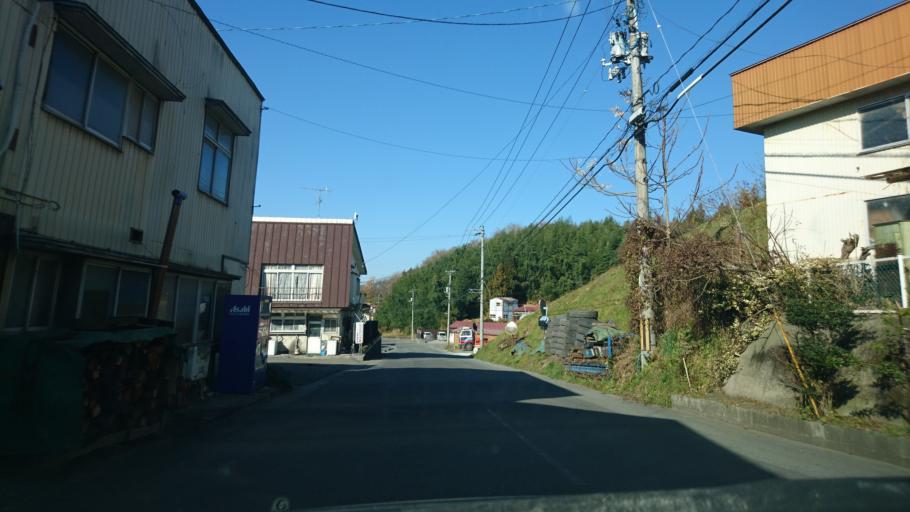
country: JP
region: Iwate
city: Ichinoseki
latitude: 38.9144
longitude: 141.3440
